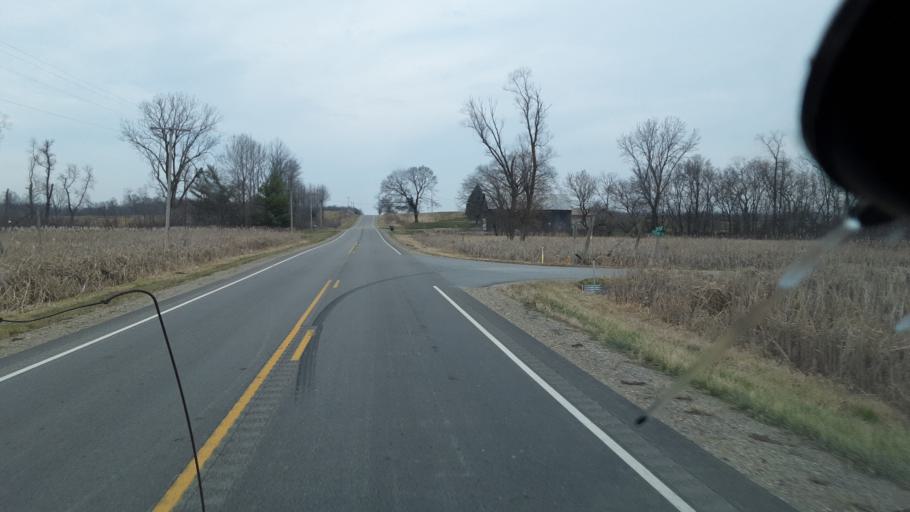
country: US
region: Indiana
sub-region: Noble County
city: Kendallville
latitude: 41.5406
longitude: -85.1707
